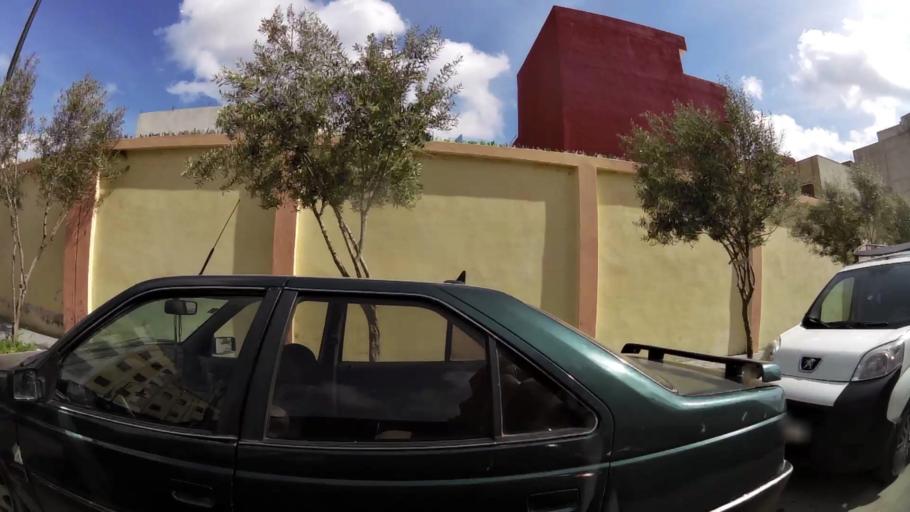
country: MA
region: Tanger-Tetouan
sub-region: Tanger-Assilah
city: Tangier
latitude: 35.7680
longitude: -5.7662
